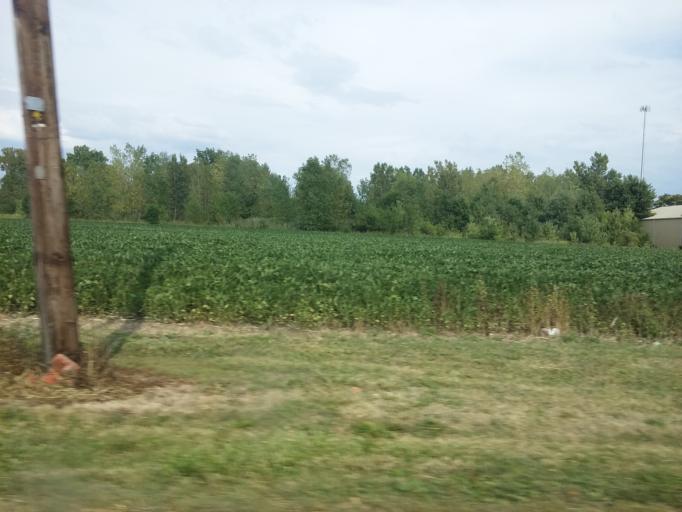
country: US
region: Ohio
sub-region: Hancock County
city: McComb
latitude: 41.1935
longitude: -83.7844
